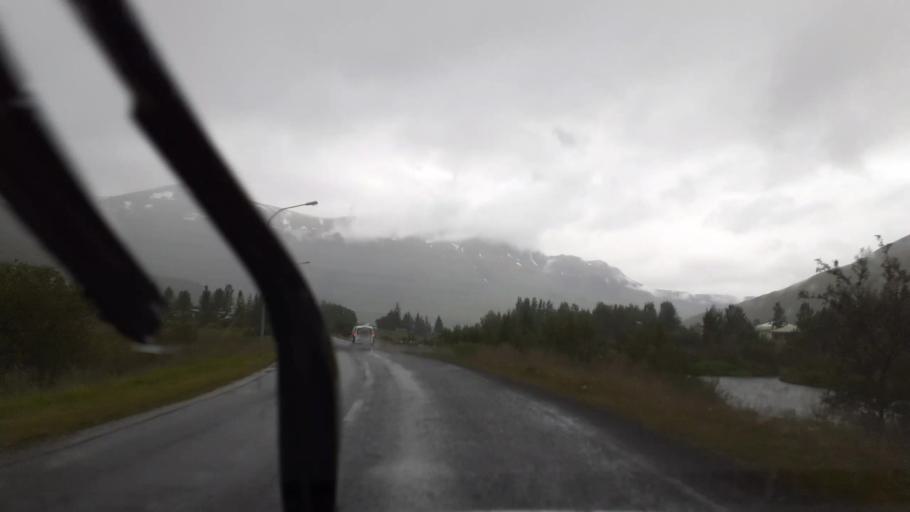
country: IS
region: East
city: Eskifjoerdur
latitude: 65.2548
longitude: -14.0136
